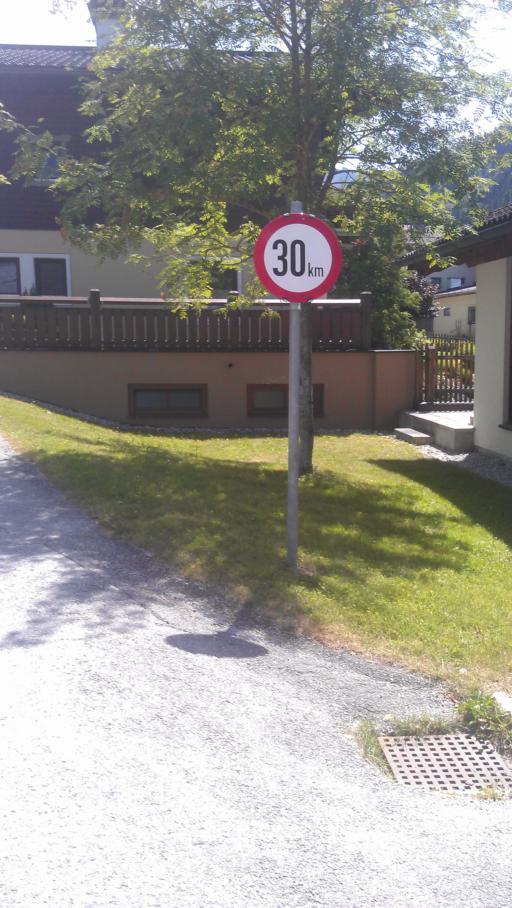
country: AT
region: Salzburg
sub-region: Politischer Bezirk Sankt Johann im Pongau
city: Kleinarl
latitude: 47.2768
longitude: 13.3198
